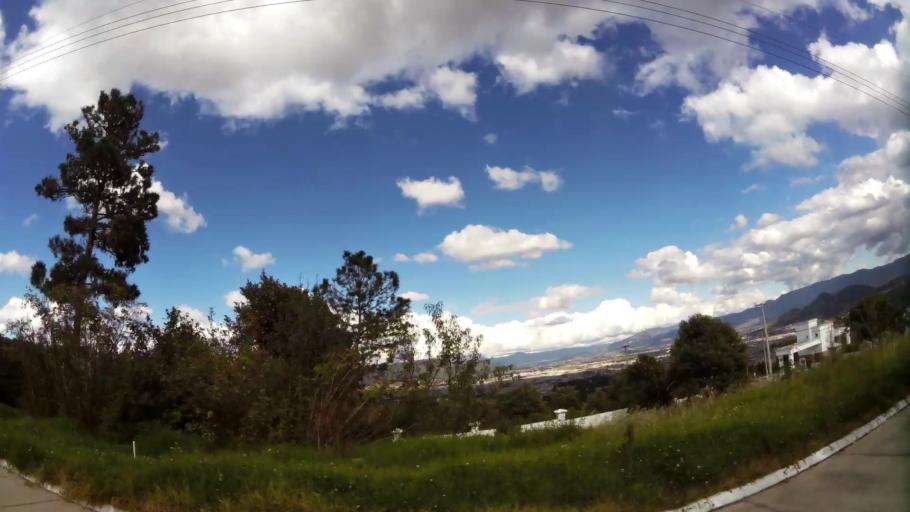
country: GT
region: Quetzaltenango
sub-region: Municipio de La Esperanza
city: La Esperanza
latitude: 14.8357
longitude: -91.5587
